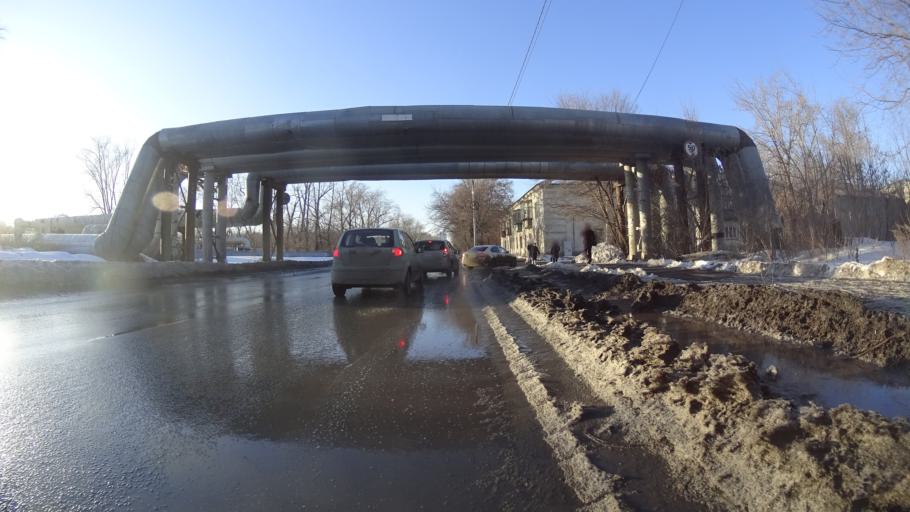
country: RU
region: Chelyabinsk
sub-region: Gorod Chelyabinsk
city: Chelyabinsk
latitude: 55.1320
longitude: 61.4625
